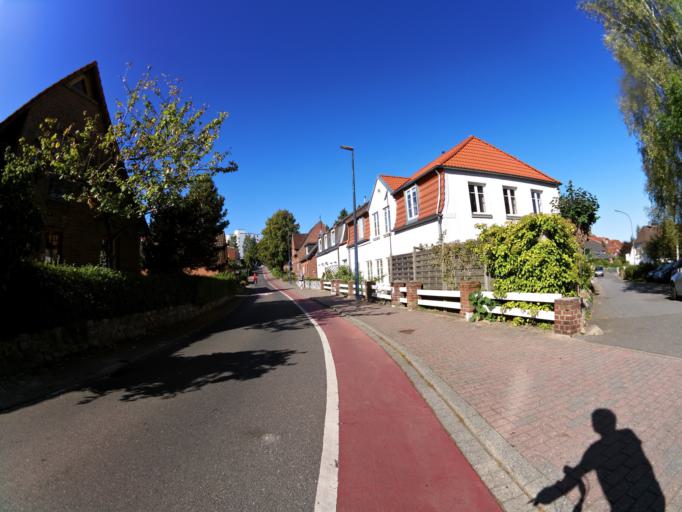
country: DE
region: Schleswig-Holstein
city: Eckernforde
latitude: 54.4801
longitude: 9.8384
